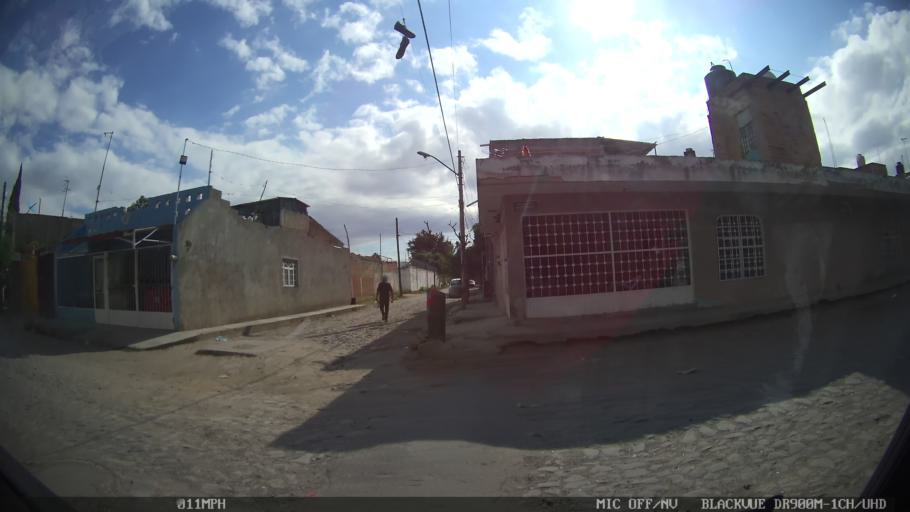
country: MX
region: Jalisco
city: Tonala
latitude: 20.6550
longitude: -103.2498
